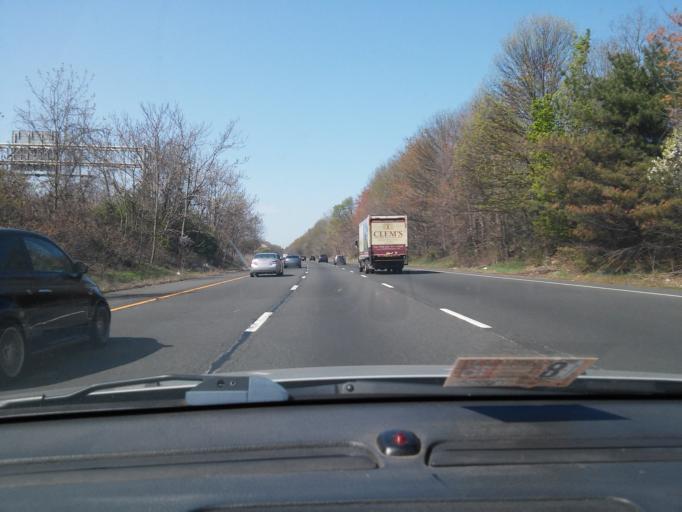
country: US
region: New Jersey
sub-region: Union County
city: Springfield
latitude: 40.7080
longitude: -74.3372
